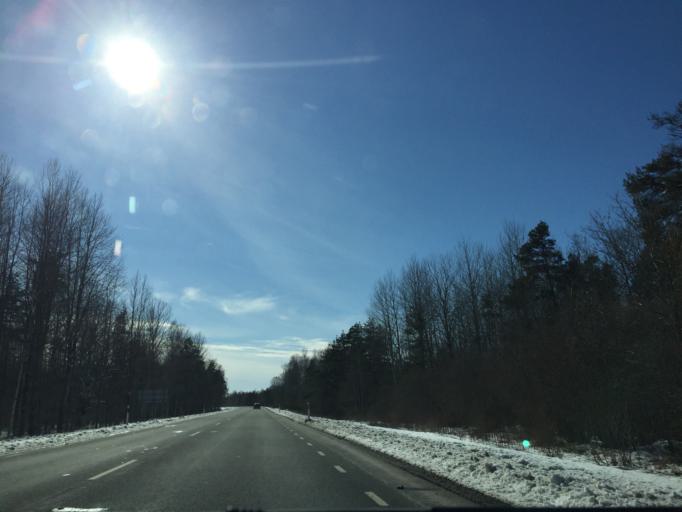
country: EE
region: Saare
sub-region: Kuressaare linn
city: Kuressaare
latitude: 58.3209
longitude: 22.6328
